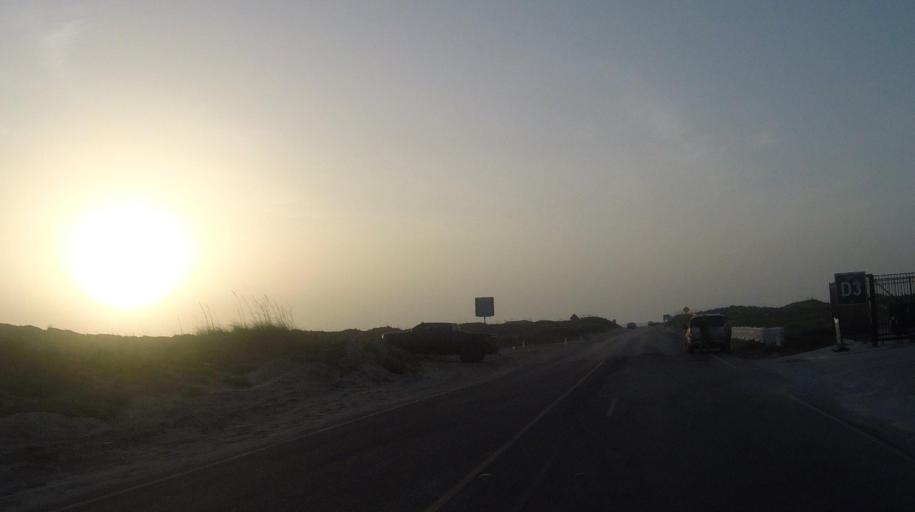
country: US
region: Texas
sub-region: Cameron County
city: Port Isabel
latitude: 25.9974
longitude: -97.1536
